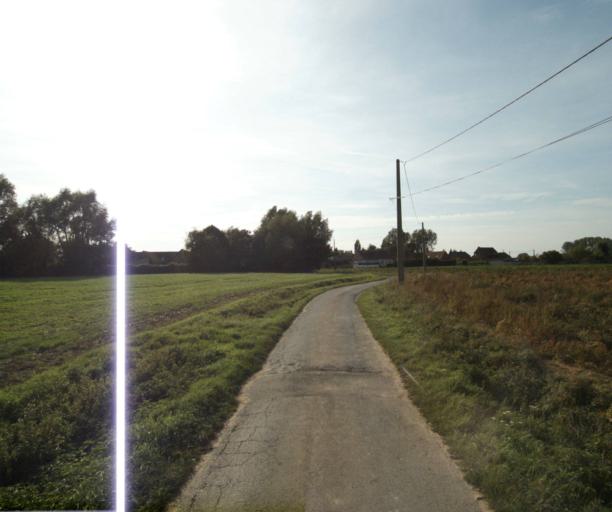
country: FR
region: Nord-Pas-de-Calais
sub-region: Departement du Nord
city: Fournes-en-Weppes
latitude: 50.5993
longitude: 2.8731
